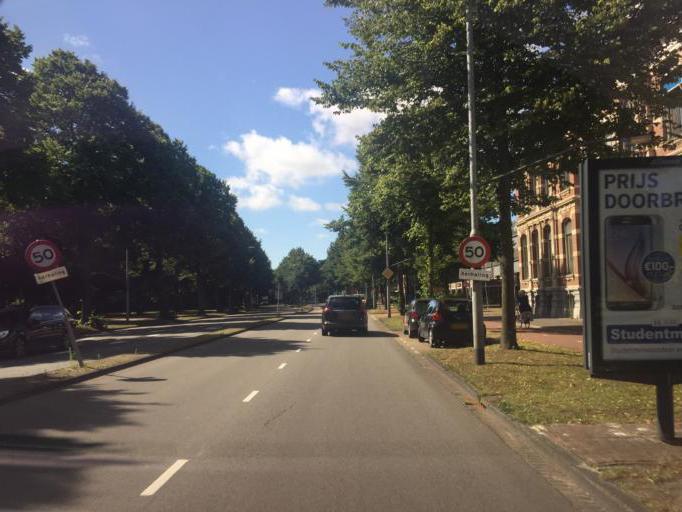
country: NL
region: North Holland
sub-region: Gemeente Haarlem
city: Haarlem
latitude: 52.3713
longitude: 4.6291
